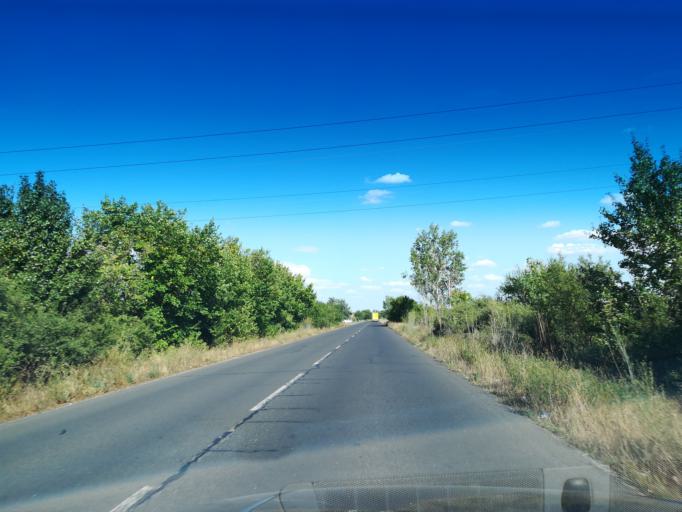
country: BG
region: Stara Zagora
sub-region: Obshtina Chirpan
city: Chirpan
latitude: 42.0715
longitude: 25.2040
